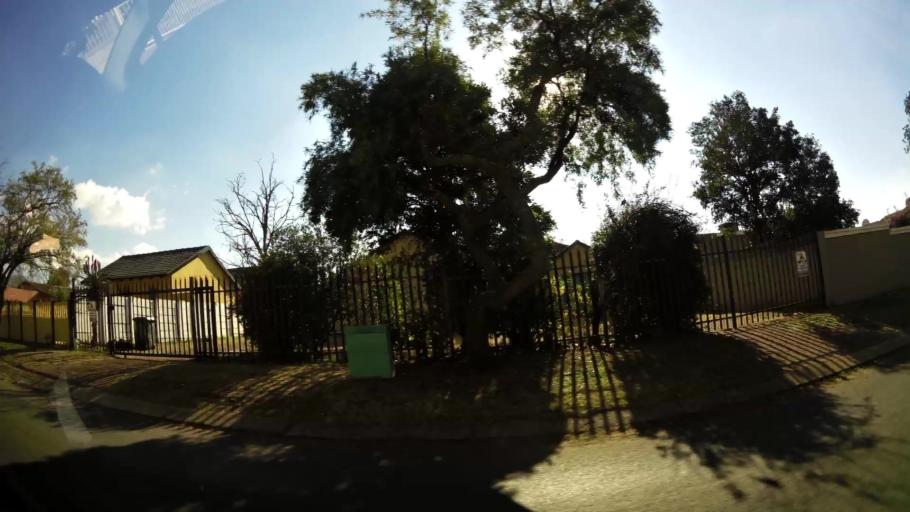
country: ZA
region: Gauteng
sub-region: City of Johannesburg Metropolitan Municipality
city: Roodepoort
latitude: -26.1628
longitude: 27.8216
